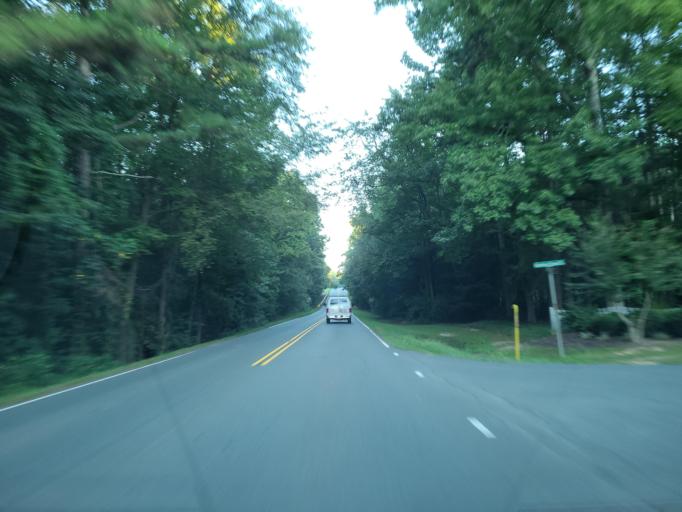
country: US
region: North Carolina
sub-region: Union County
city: Weddington
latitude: 35.0139
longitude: -80.7461
